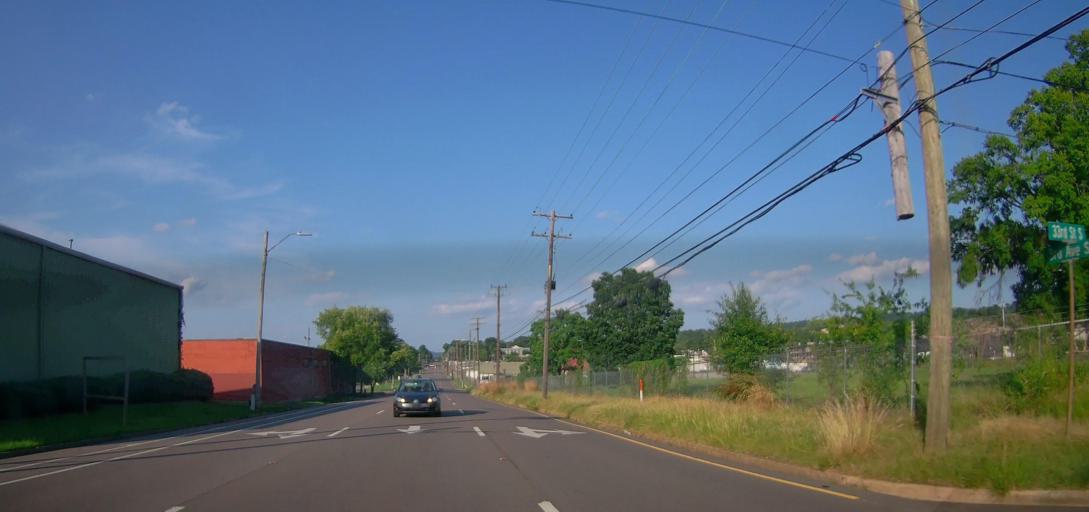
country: US
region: Alabama
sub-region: Jefferson County
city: Birmingham
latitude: 33.5185
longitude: -86.7847
